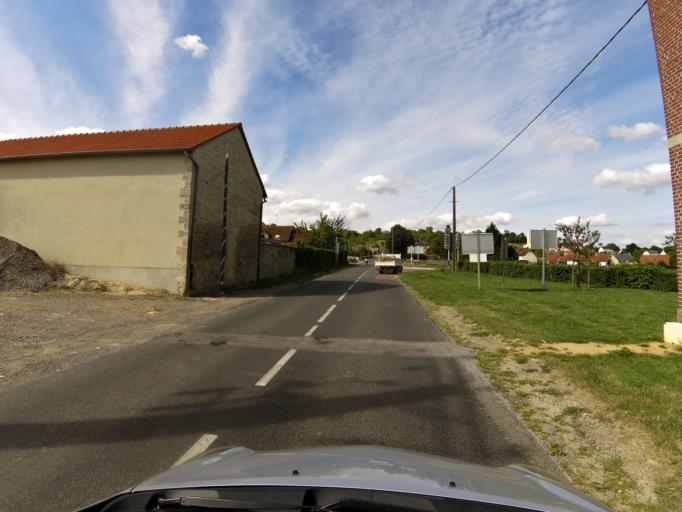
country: FR
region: Picardie
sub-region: Departement de l'Aisne
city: Bruyeres-et-Montberault
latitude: 49.4710
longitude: 3.6649
